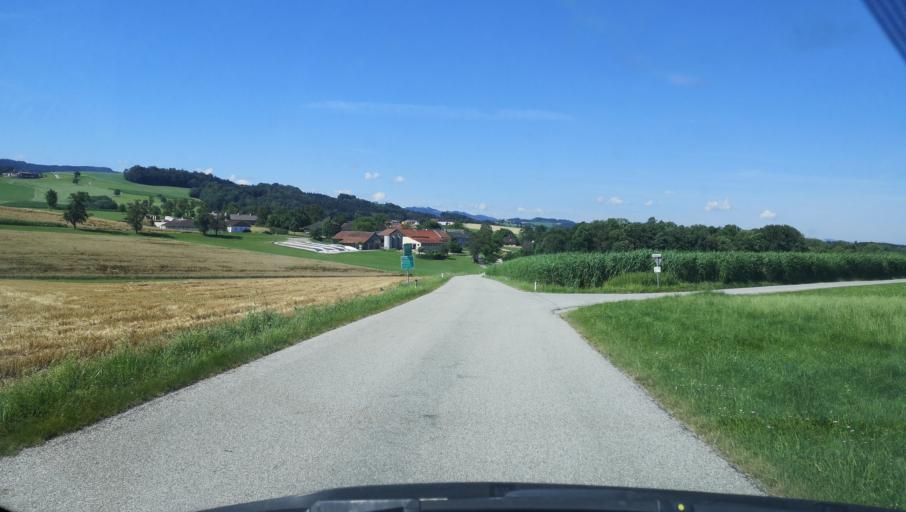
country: AT
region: Lower Austria
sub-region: Politischer Bezirk Amstetten
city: Euratsfeld
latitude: 48.0688
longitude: 14.9289
